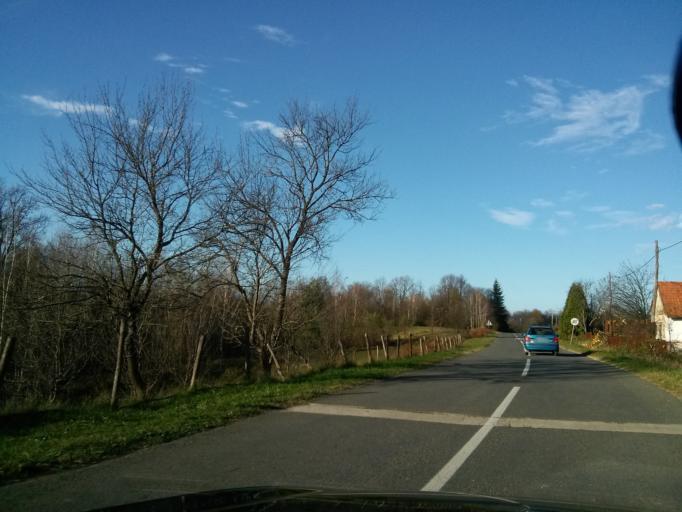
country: HR
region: Sisacko-Moslavacka
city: Gvozd
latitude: 45.3533
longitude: 15.9075
